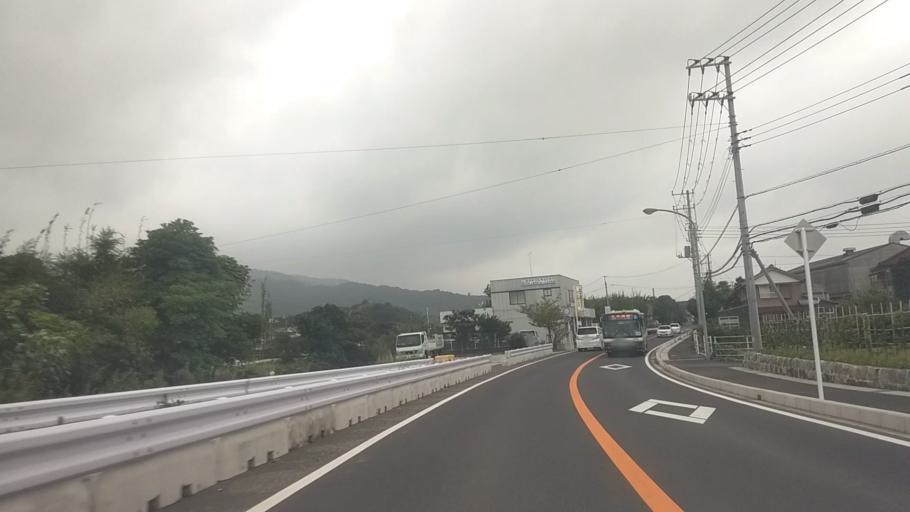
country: JP
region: Chiba
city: Kawaguchi
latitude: 35.1089
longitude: 140.0859
